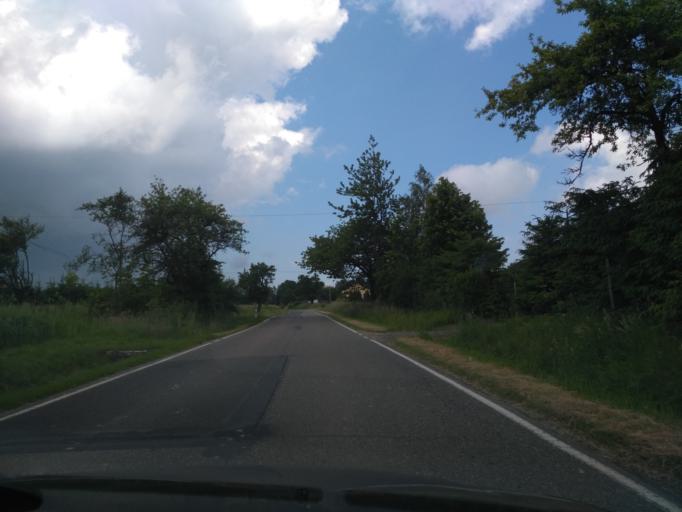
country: PL
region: Subcarpathian Voivodeship
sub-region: Powiat lancucki
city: Handzlowka
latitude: 49.9599
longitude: 22.1975
